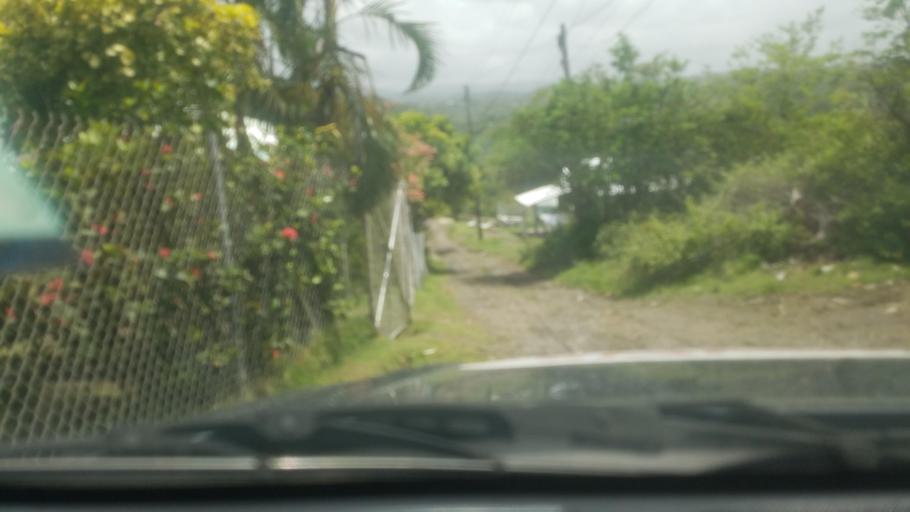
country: LC
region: Laborie Quarter
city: Laborie
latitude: 13.7502
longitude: -60.9893
